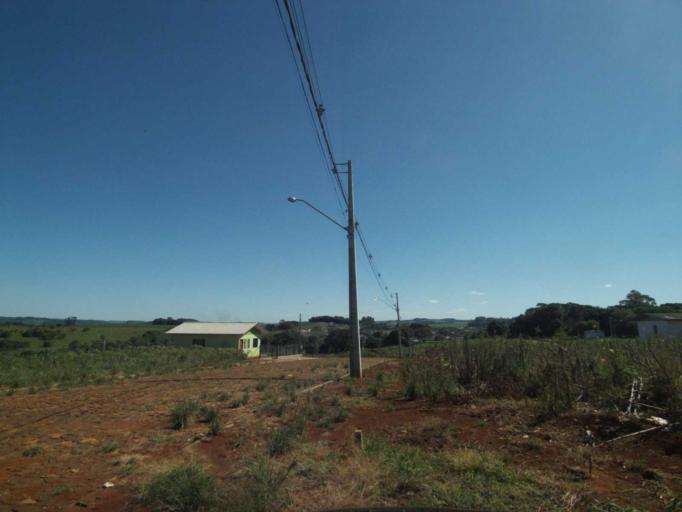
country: BR
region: Parana
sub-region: Coronel Vivida
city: Coronel Vivida
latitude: -25.9602
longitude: -52.8075
